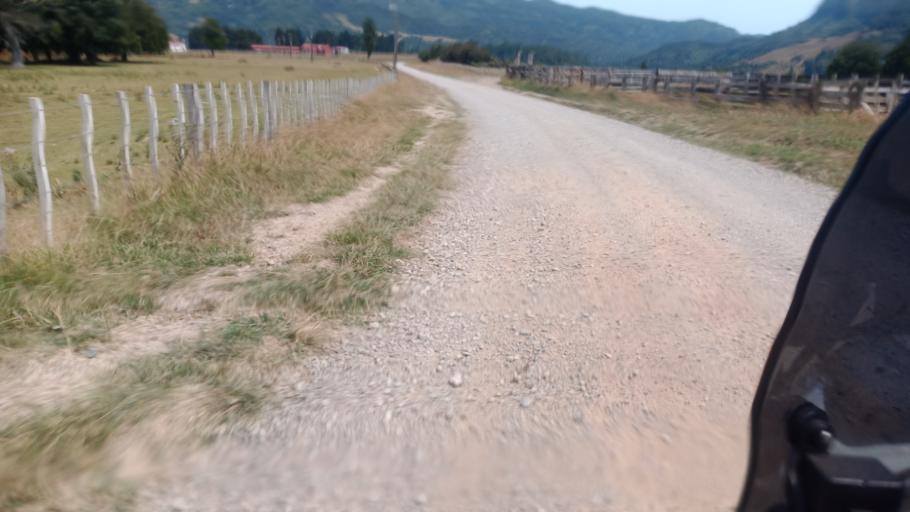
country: NZ
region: Bay of Plenty
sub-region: Opotiki District
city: Opotiki
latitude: -37.6564
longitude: 178.1163
